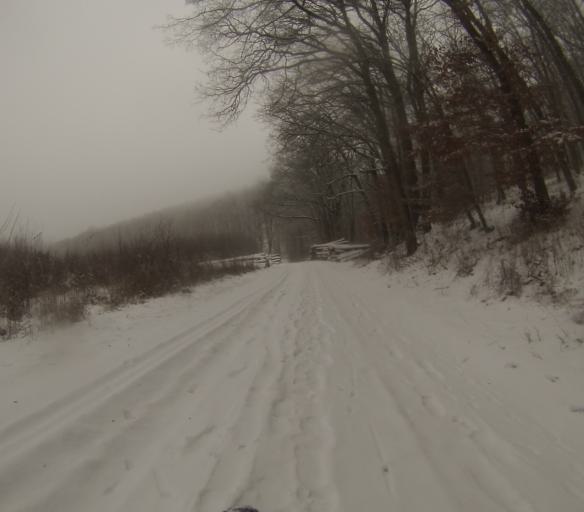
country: CZ
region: South Moravian
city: Strelice
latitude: 49.1365
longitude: 16.5191
